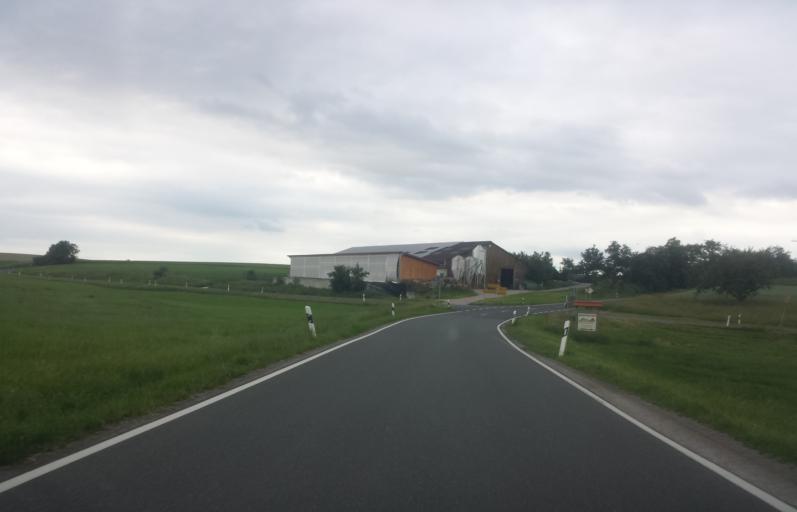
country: DE
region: Bavaria
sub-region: Regierungsbezirk Mittelfranken
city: Baudenbach
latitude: 49.6495
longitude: 10.5621
